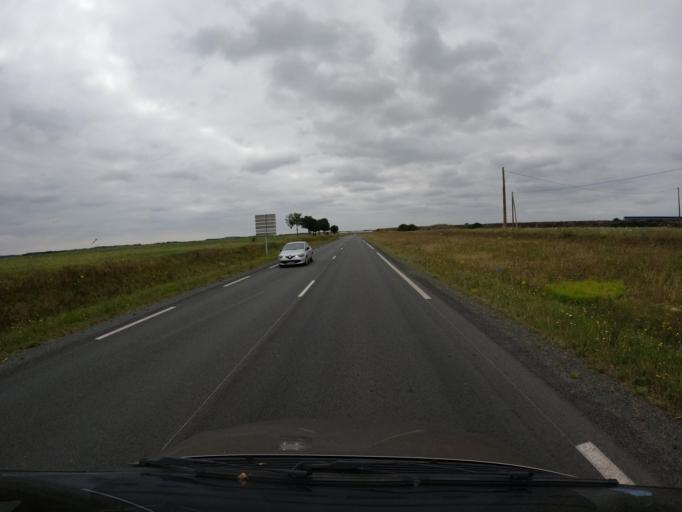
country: FR
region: Pays de la Loire
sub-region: Departement de la Vendee
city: Fontenay-le-Comte
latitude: 46.4433
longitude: -0.7916
